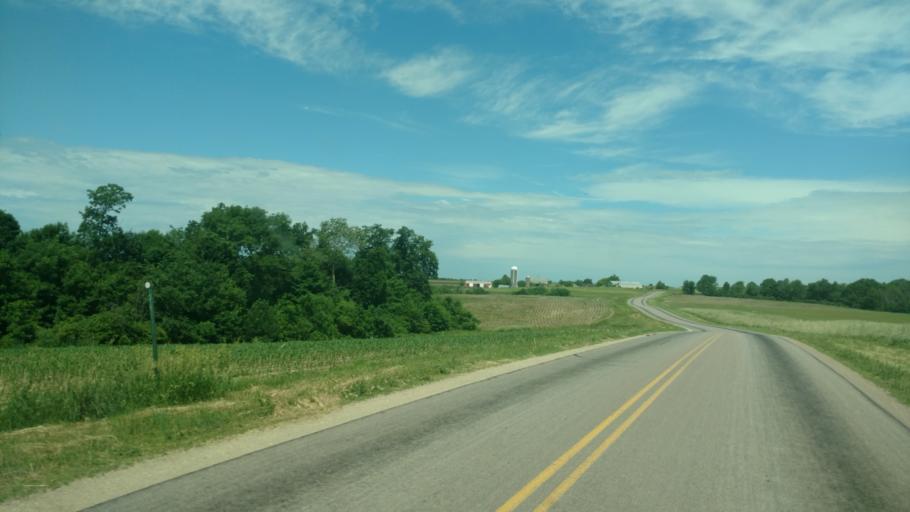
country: US
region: Wisconsin
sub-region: Vernon County
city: Hillsboro
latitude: 43.5987
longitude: -90.4171
